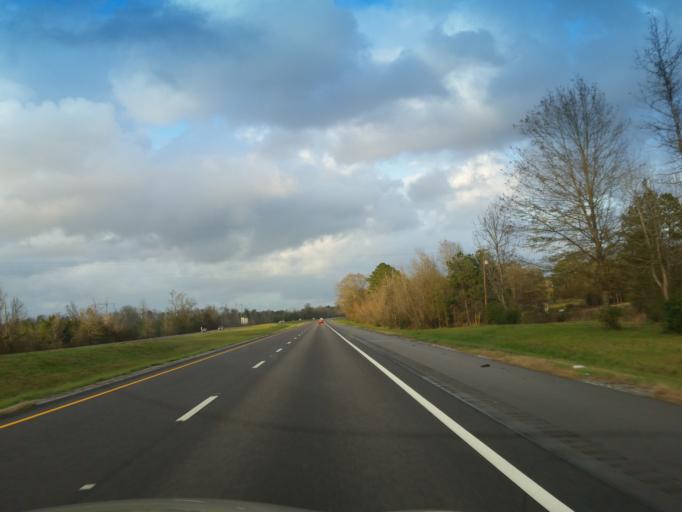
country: US
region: Mississippi
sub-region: Jones County
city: Sharon
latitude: 31.9168
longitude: -89.0058
